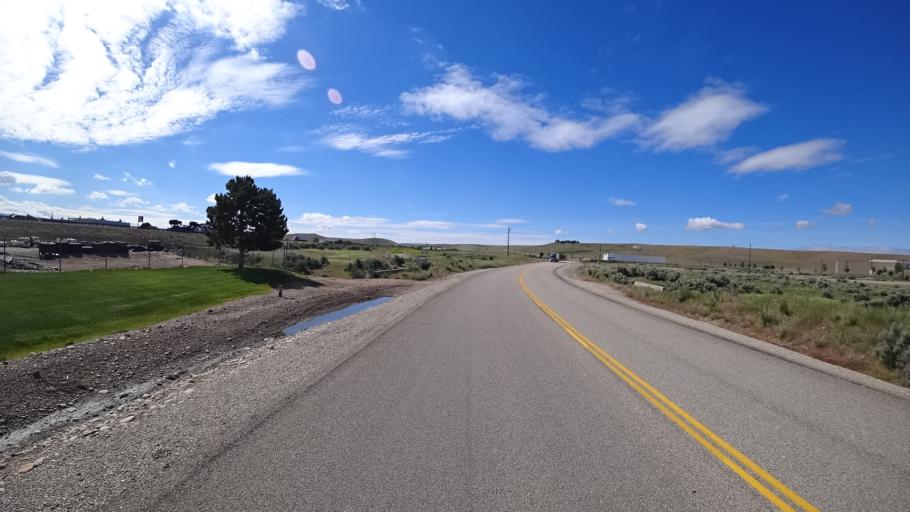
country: US
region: Idaho
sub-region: Ada County
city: Boise
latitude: 43.5218
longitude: -116.1514
